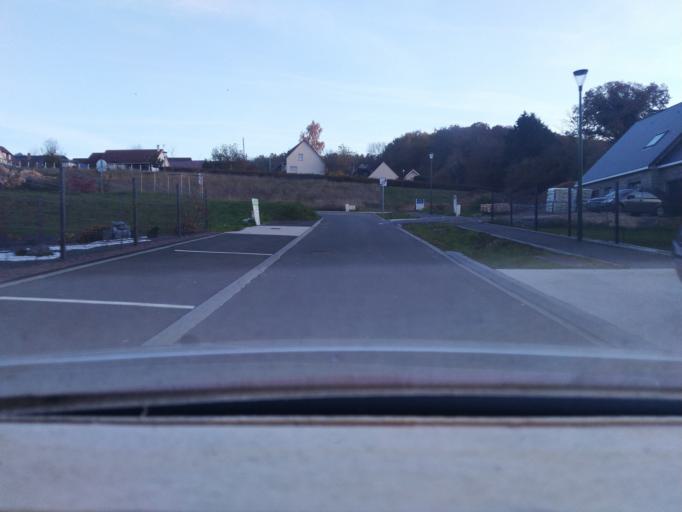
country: FR
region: Haute-Normandie
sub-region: Departement de la Seine-Maritime
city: Yainville
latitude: 49.4563
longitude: 0.8338
